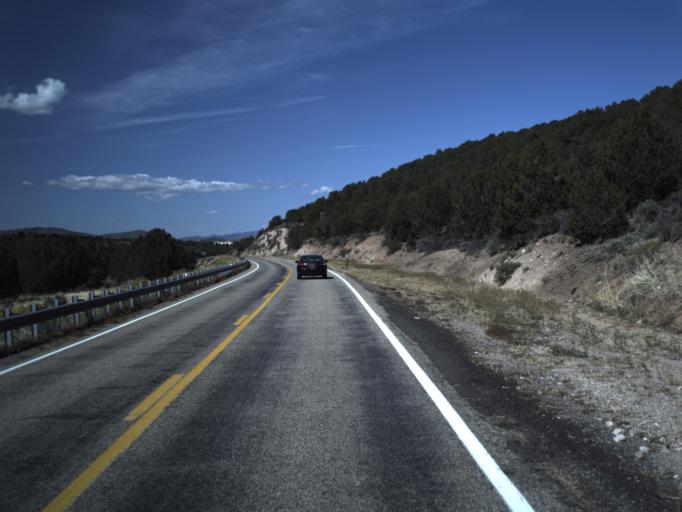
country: US
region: Utah
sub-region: Washington County
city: Enterprise
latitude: 37.5499
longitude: -113.6862
